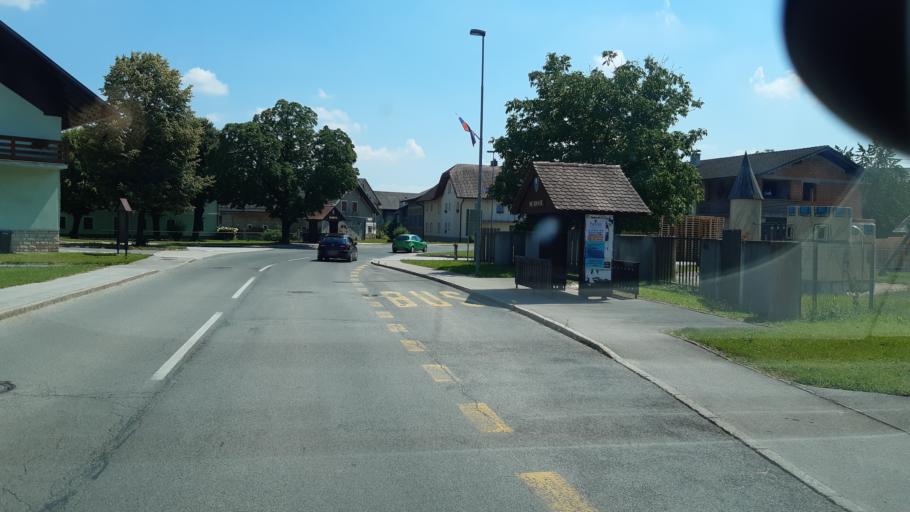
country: SI
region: Cerklje na Gorenjskem
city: Cerklje na Gorenjskem
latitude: 46.2308
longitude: 14.4874
